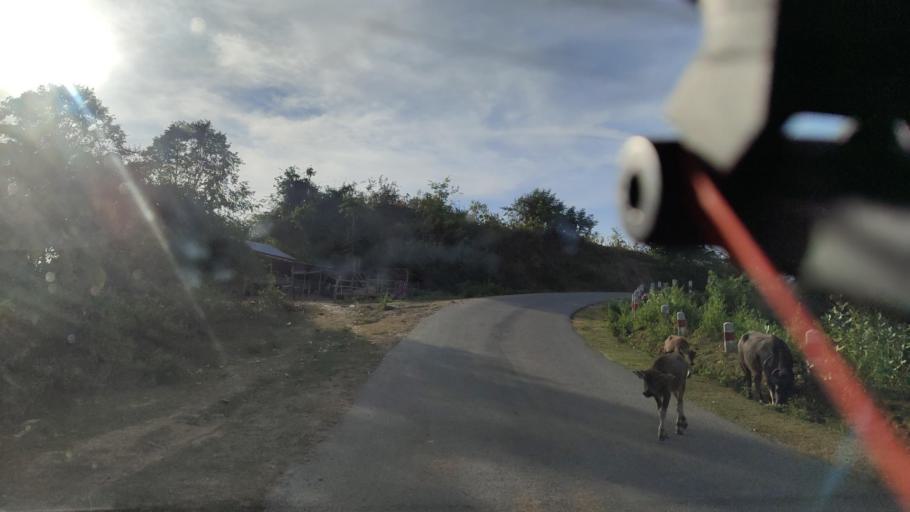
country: MM
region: Magway
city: Taungdwingyi
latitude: 20.0145
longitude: 95.8340
